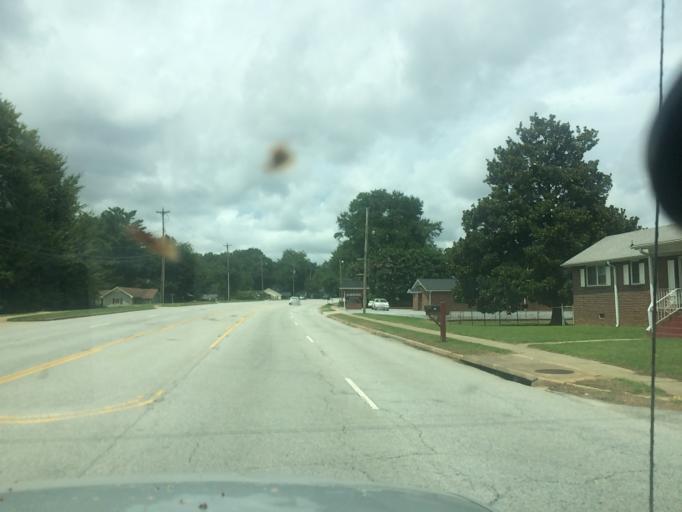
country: US
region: South Carolina
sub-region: Greenville County
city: Greer
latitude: 34.9247
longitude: -82.2196
